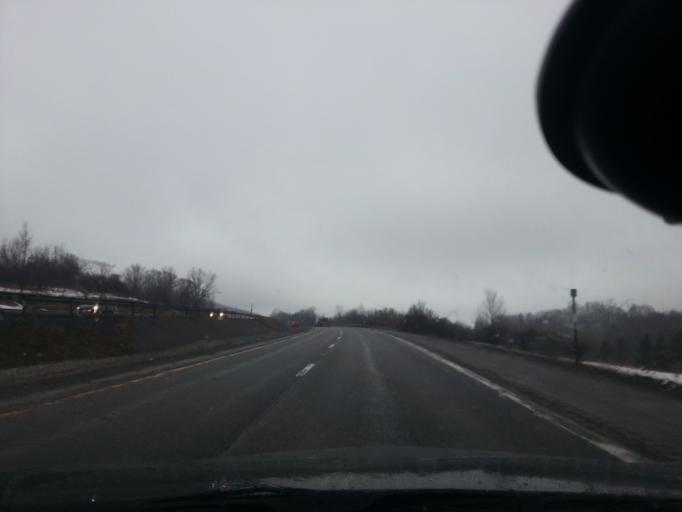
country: US
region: New York
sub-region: Onondaga County
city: Nedrow
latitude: 42.8172
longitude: -76.1254
